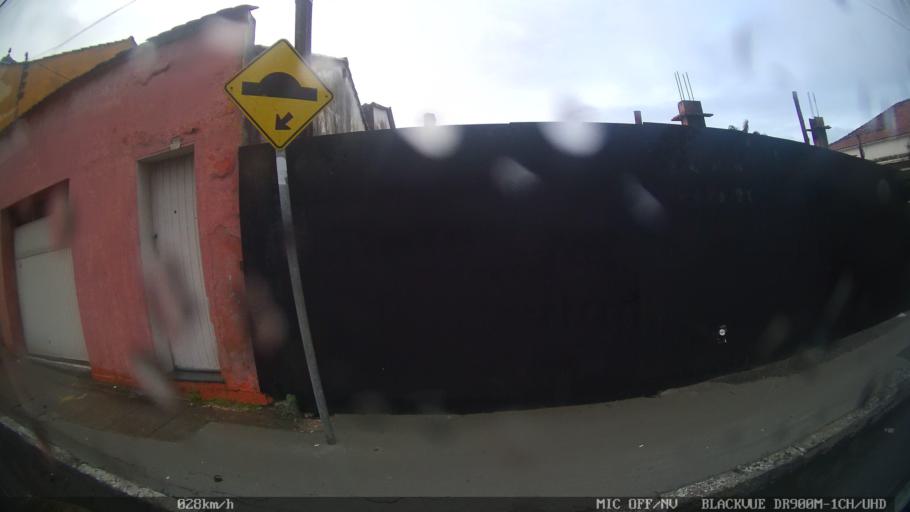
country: BR
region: Santa Catarina
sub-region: Sao Jose
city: Campinas
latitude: -27.6149
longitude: -48.6264
